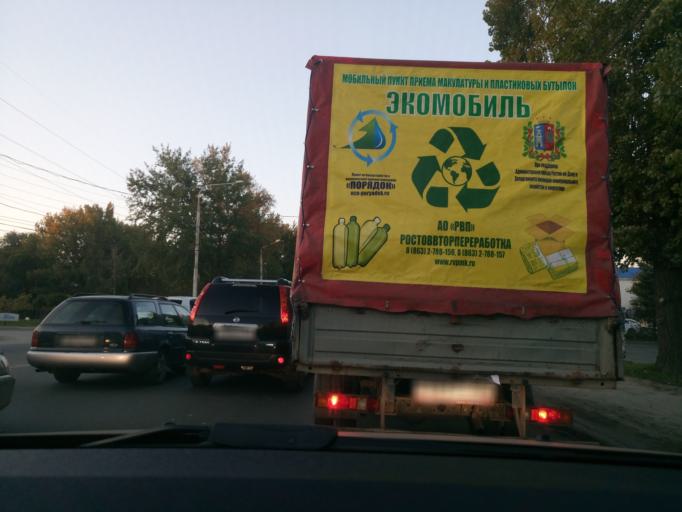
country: RU
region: Rostov
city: Kalinin
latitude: 47.2417
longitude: 39.6141
